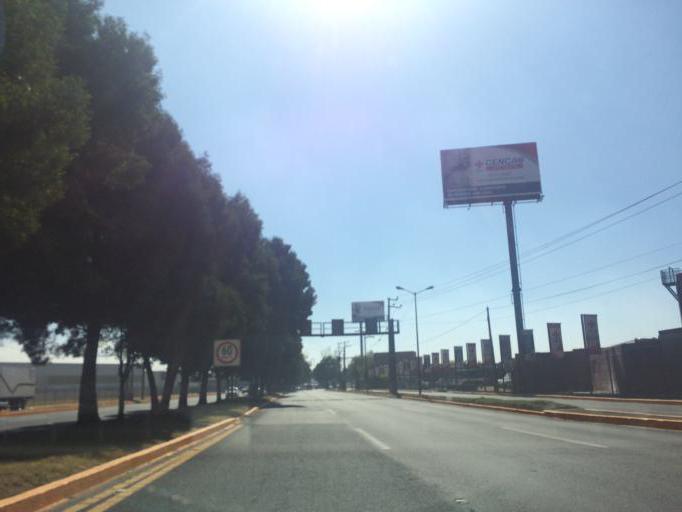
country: MX
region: Mexico
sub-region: Toluca
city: Guadalupe Totoltepec
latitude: 19.3339
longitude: -99.5723
